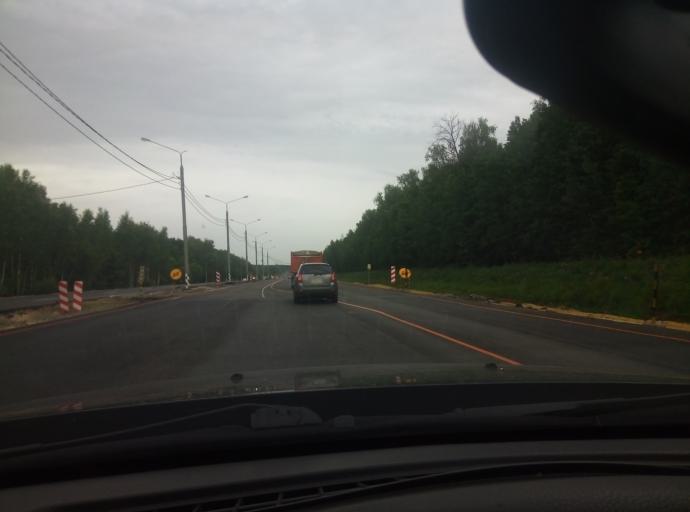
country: RU
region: Tula
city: Zaokskiy
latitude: 54.5967
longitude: 37.5003
